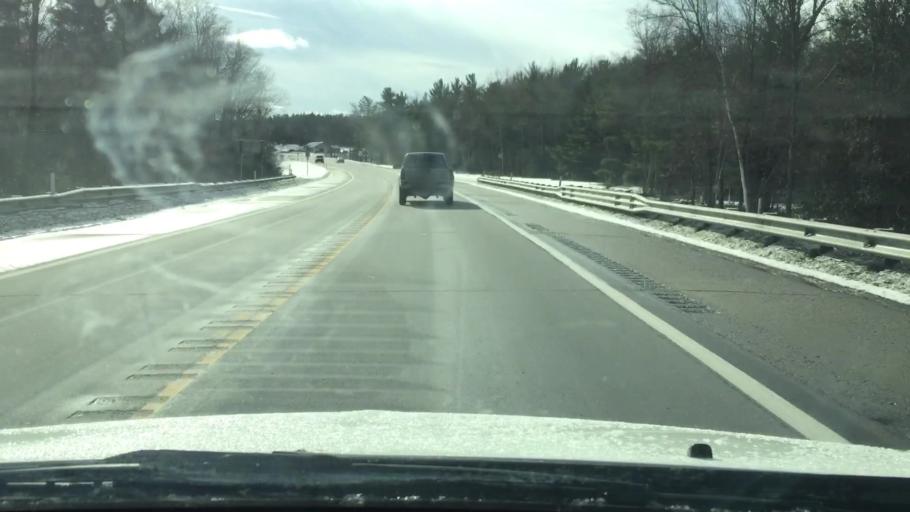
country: US
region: Michigan
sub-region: Kalkaska County
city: Kalkaska
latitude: 44.6441
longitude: -85.2829
